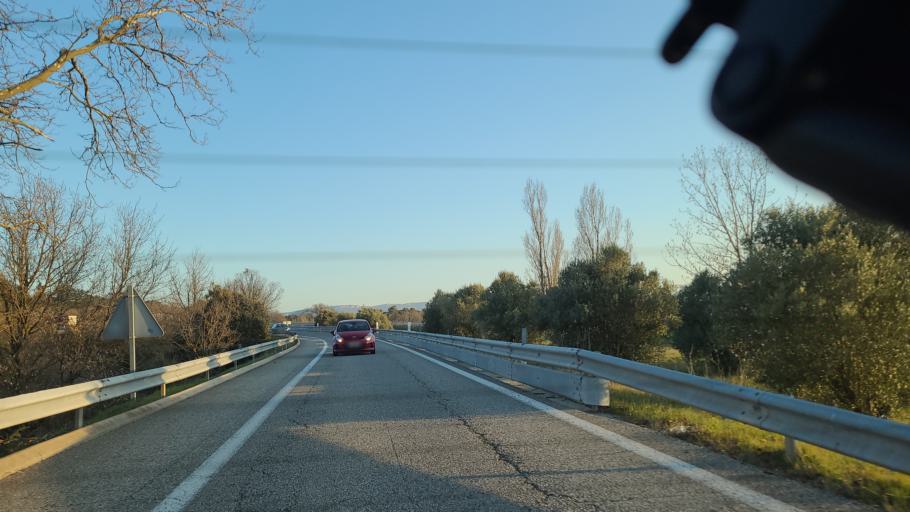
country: FR
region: Provence-Alpes-Cote d'Azur
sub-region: Departement du Var
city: Saint-Maximin-la-Sainte-Baume
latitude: 43.4512
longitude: 5.8857
